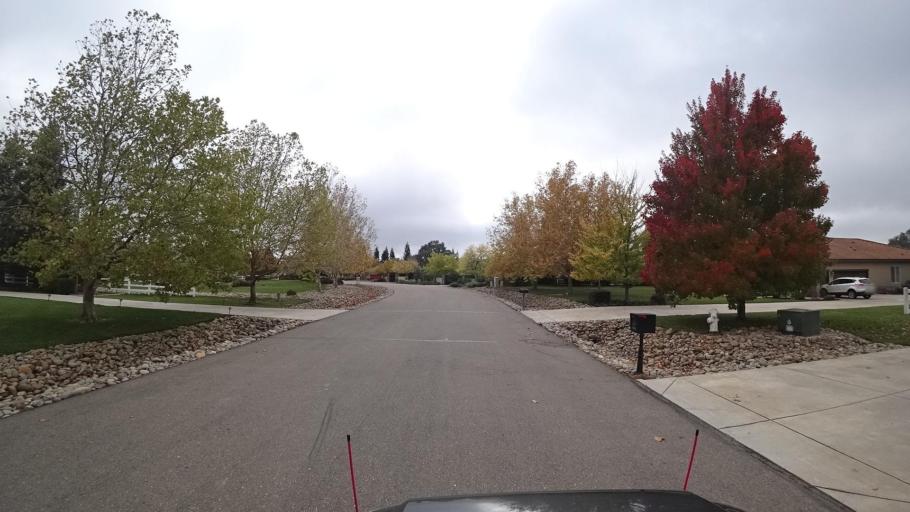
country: US
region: California
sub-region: Sacramento County
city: Vineyard
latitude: 38.4487
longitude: -121.3127
